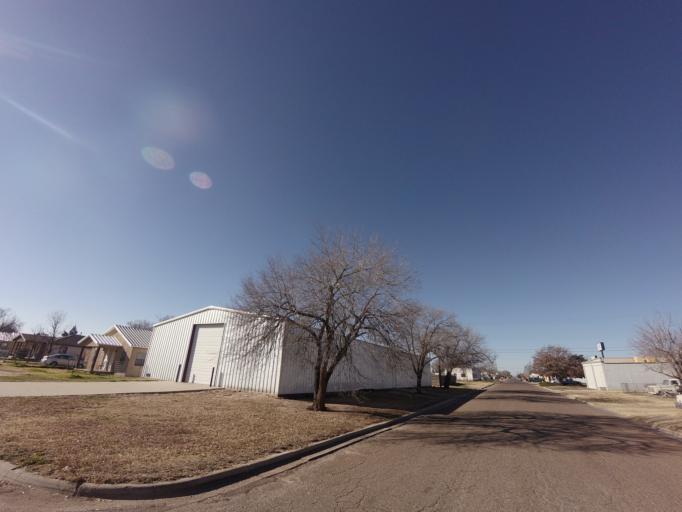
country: US
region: New Mexico
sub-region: Curry County
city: Clovis
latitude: 34.4039
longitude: -103.1953
